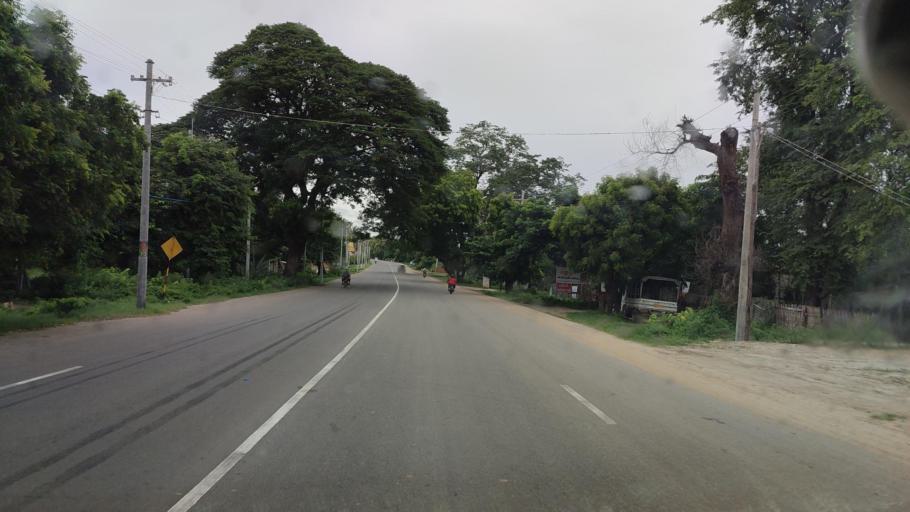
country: MM
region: Mandalay
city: Meiktila
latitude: 20.7963
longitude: 95.9113
